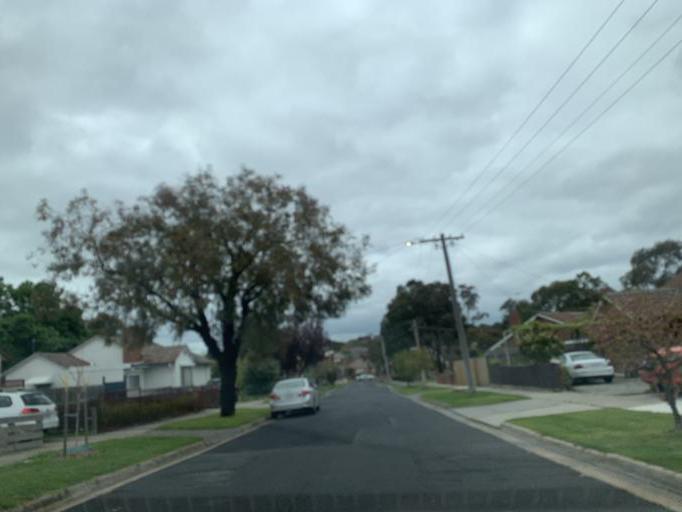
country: AU
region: Victoria
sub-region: Moreland
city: Coburg North
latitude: -37.7330
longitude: 144.9817
